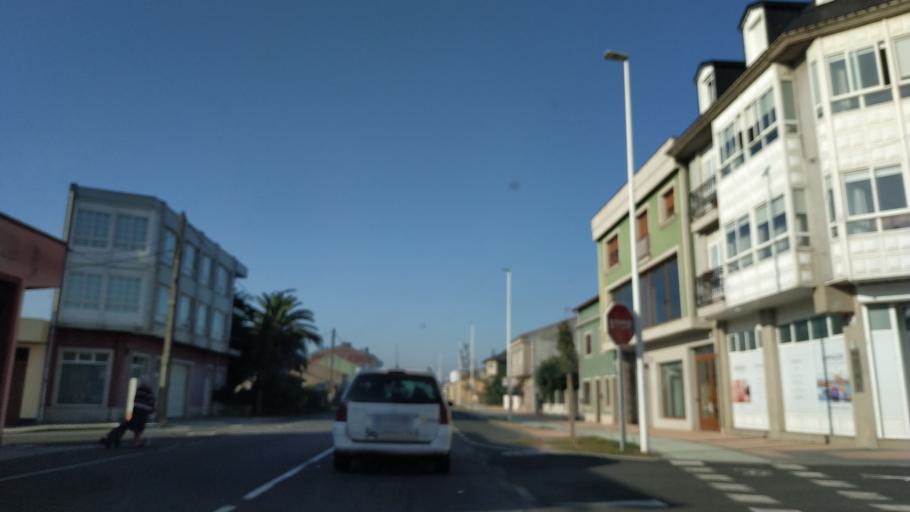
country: ES
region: Galicia
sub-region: Provincia da Coruna
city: Carballo
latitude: 43.2253
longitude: -8.6794
